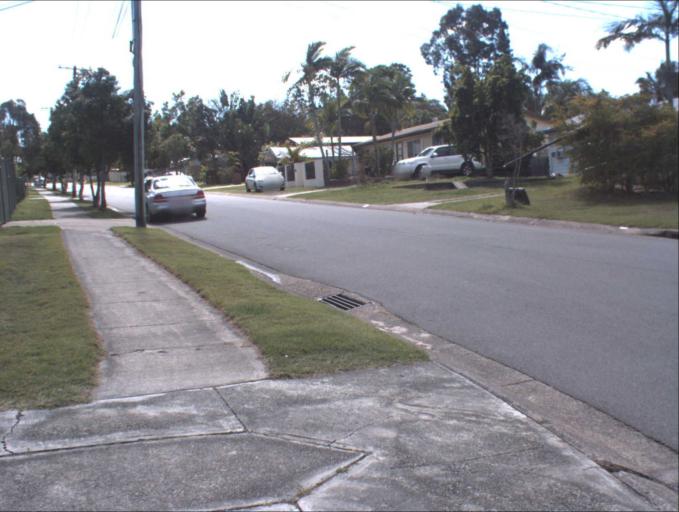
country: AU
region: Queensland
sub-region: Logan
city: Logan Reserve
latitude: -27.6900
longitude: 153.0980
